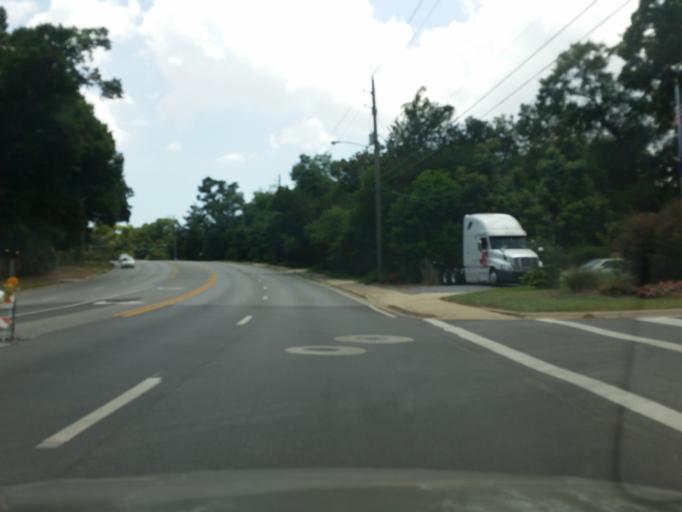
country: US
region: Florida
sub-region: Escambia County
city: Goulding
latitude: 30.4593
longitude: -87.2096
